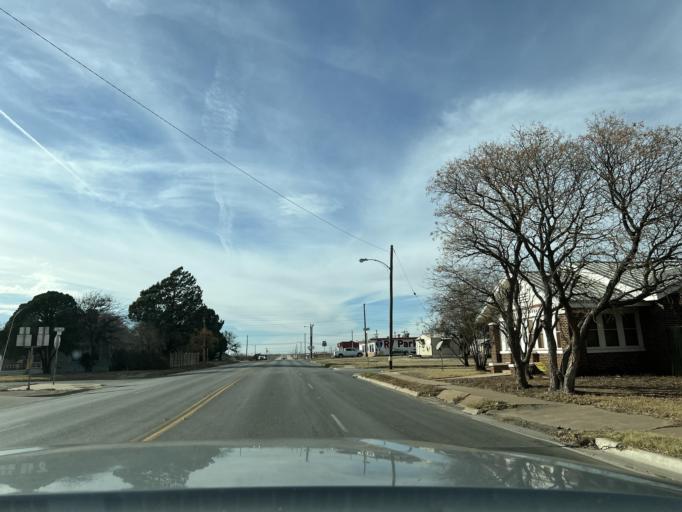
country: US
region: Texas
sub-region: Jones County
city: Anson
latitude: 32.7516
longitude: -99.8976
